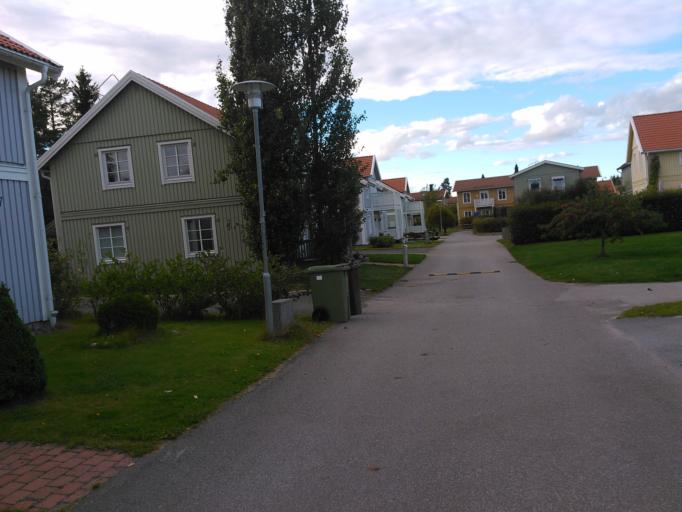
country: SE
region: Vaesterbotten
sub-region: Umea Kommun
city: Ersmark
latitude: 63.8054
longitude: 20.3385
